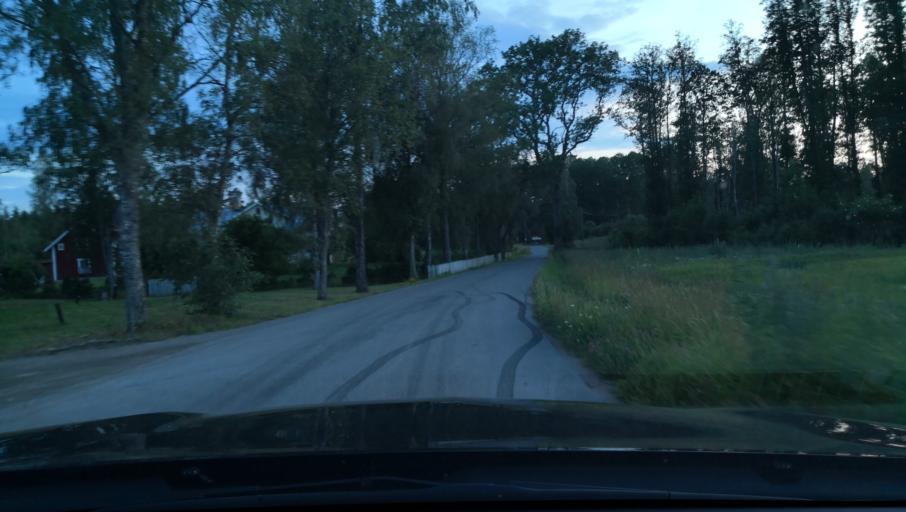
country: SE
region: Uppsala
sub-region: Osthammars Kommun
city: Bjorklinge
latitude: 60.0329
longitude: 17.4661
